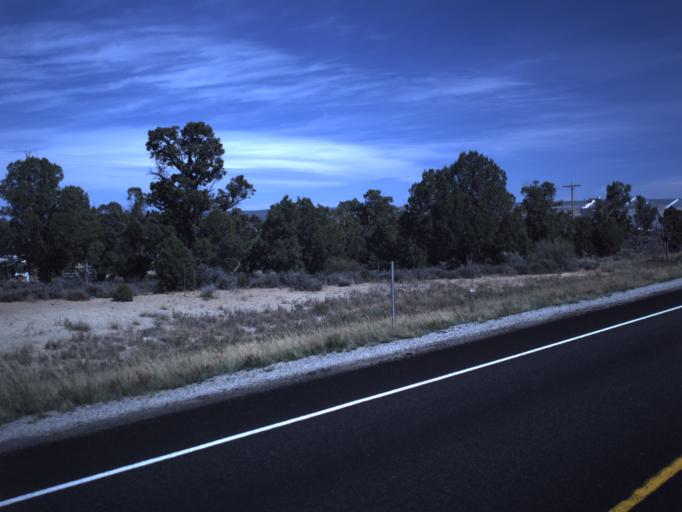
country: US
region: Colorado
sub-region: Dolores County
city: Dove Creek
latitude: 37.8356
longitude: -109.1087
